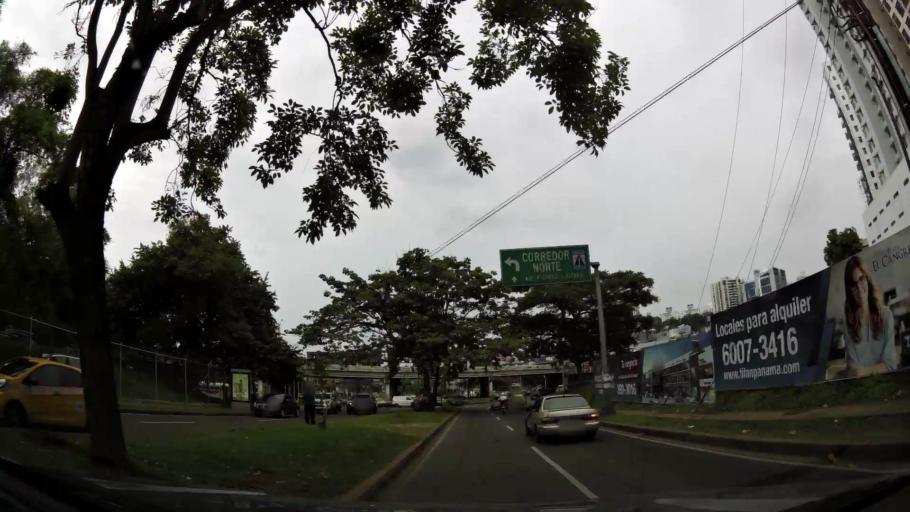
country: PA
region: Panama
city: Panama
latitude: 8.9879
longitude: -79.5323
